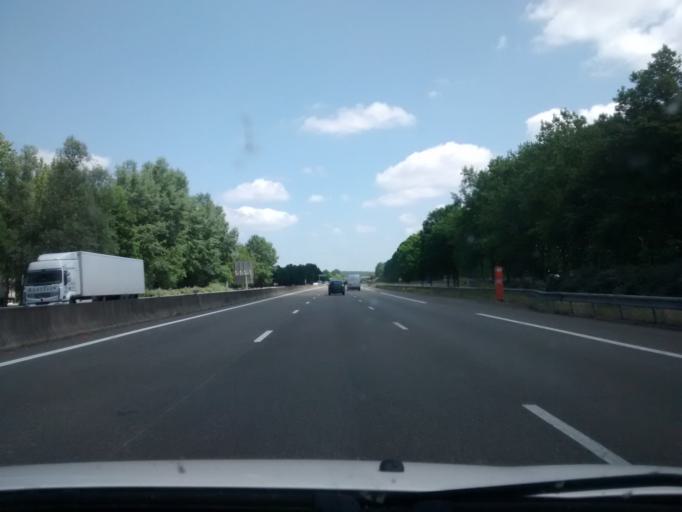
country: FR
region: Pays de la Loire
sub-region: Departement de la Sarthe
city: Champagne
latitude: 48.0533
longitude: 0.3291
